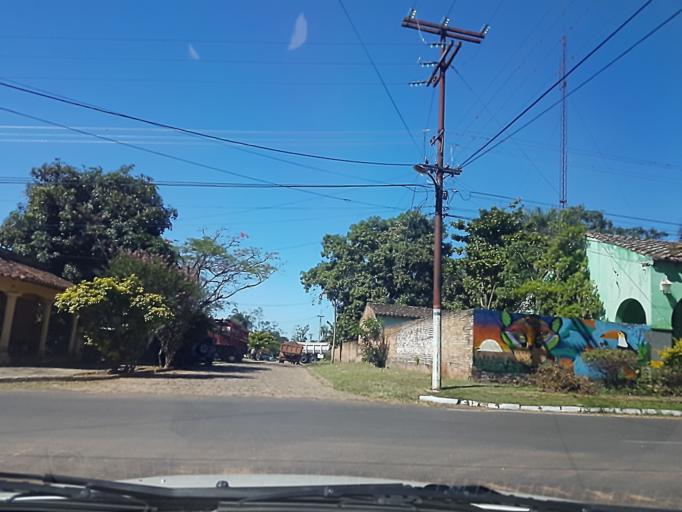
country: PY
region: Cordillera
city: Atyra
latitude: -25.2762
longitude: -57.1720
